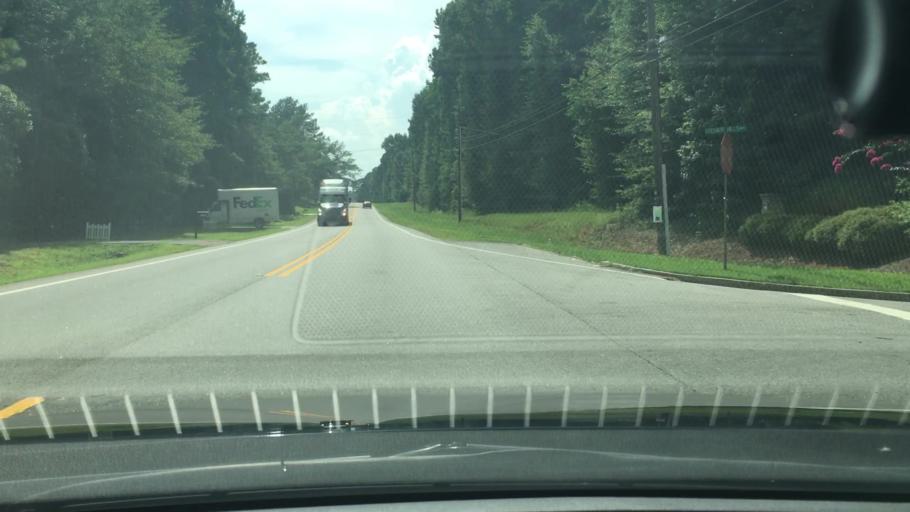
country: US
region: Georgia
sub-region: Coweta County
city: East Newnan
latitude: 33.3356
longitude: -84.7234
